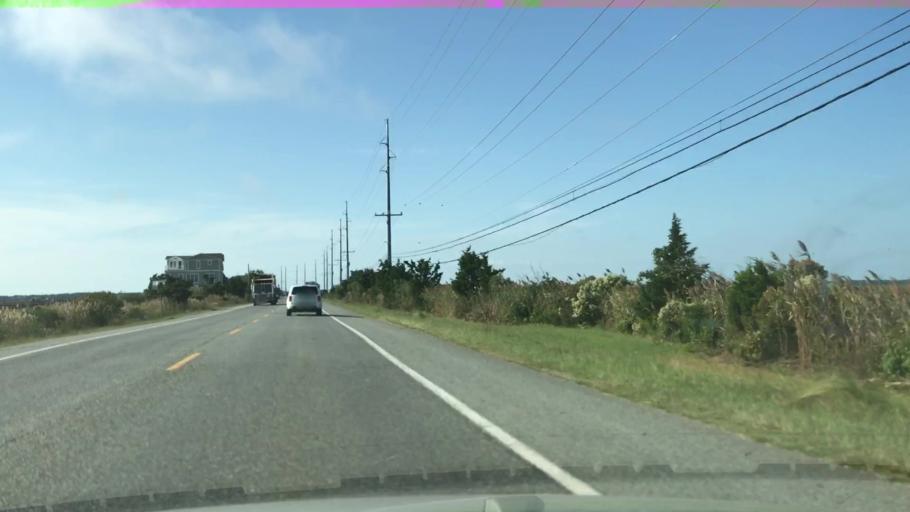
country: US
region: New Jersey
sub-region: Cape May County
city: Cape May Court House
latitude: 39.0635
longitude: -74.7764
